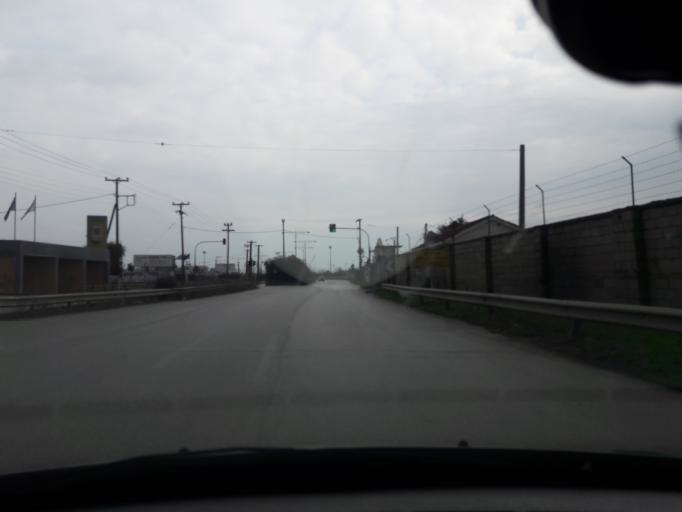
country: GR
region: Central Macedonia
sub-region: Nomos Thessalonikis
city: Menemeni
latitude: 40.6510
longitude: 22.9018
